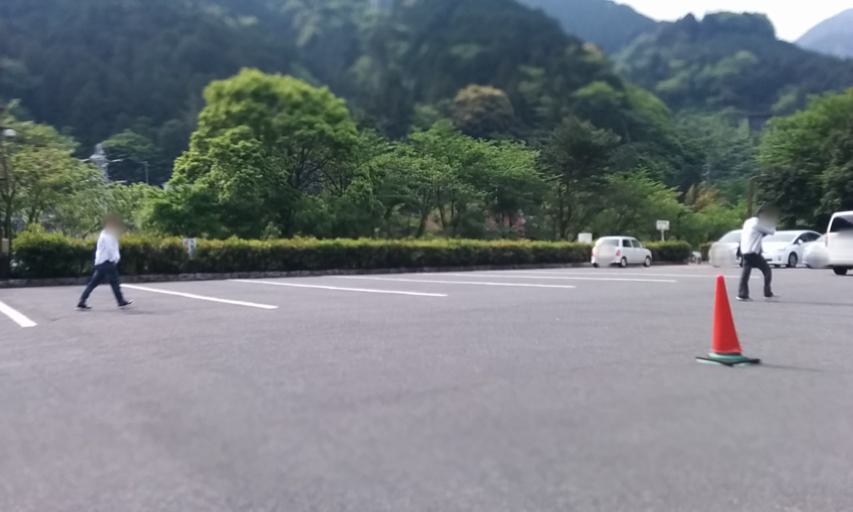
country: JP
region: Ehime
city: Niihama
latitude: 33.9027
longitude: 133.3100
